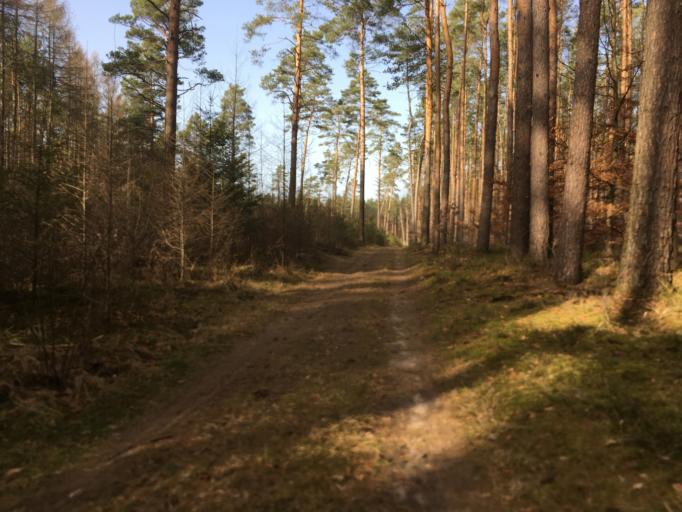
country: DE
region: Brandenburg
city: Bernau bei Berlin
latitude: 52.7059
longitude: 13.5260
